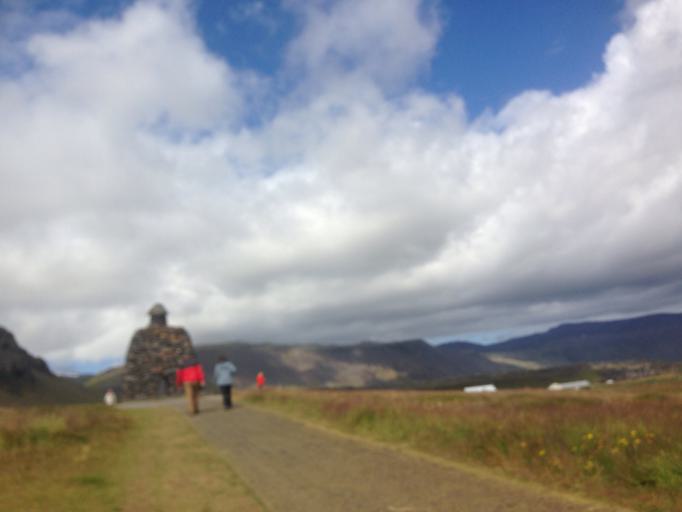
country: IS
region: West
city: Olafsvik
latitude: 64.7654
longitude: -23.6267
